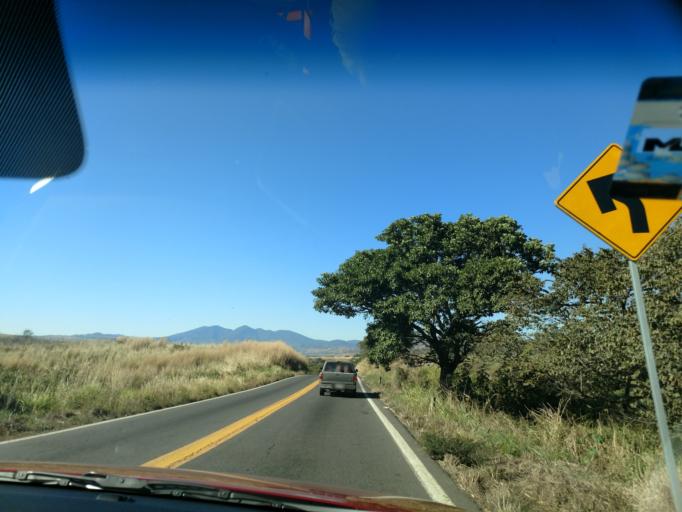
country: MX
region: Nayarit
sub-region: Ahuacatlan
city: Ahuacatlan
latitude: 21.1205
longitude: -104.5933
